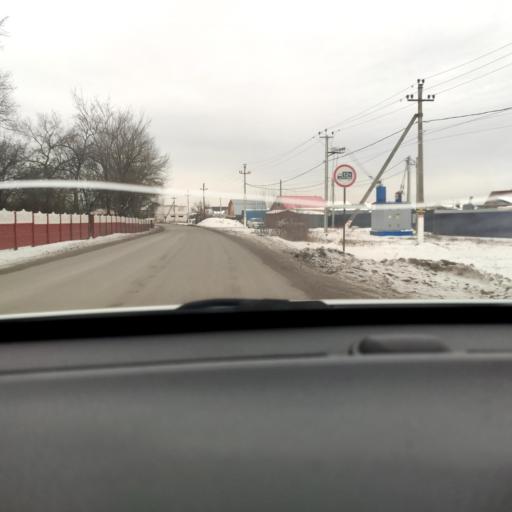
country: RU
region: Voronezj
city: Novaya Usman'
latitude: 51.6709
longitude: 39.3406
